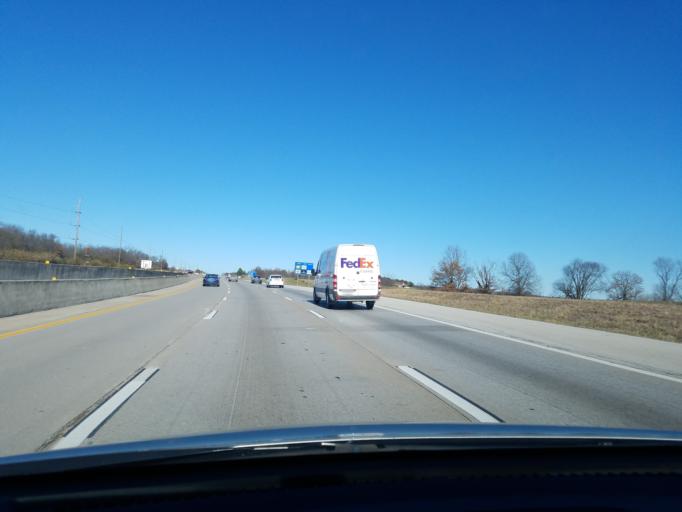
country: US
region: Missouri
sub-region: Greene County
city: Springfield
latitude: 37.1385
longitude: -93.2247
